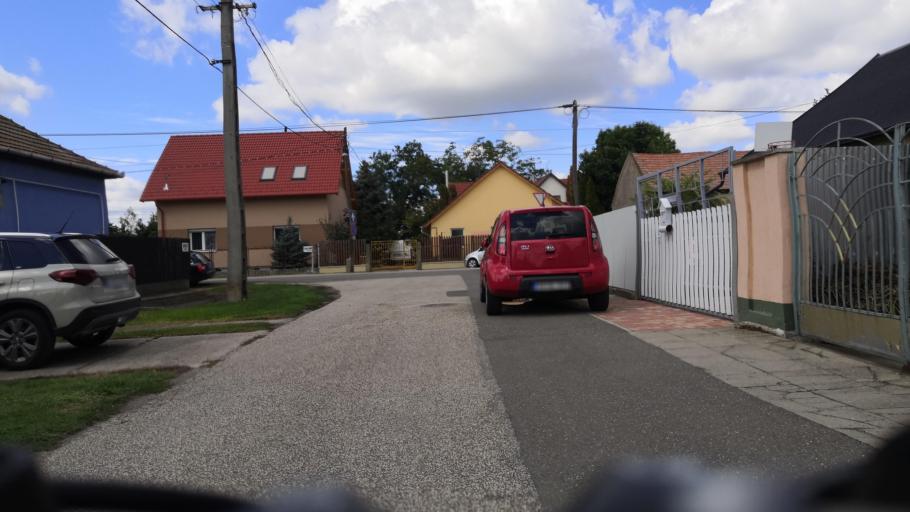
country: HU
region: Csongrad
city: Szeged
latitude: 46.2781
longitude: 20.1211
